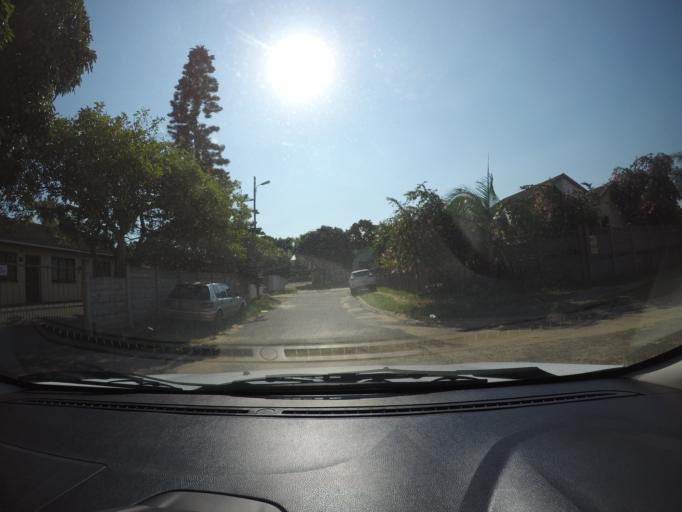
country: ZA
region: KwaZulu-Natal
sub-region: uThungulu District Municipality
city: Richards Bay
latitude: -28.7197
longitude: 32.0442
